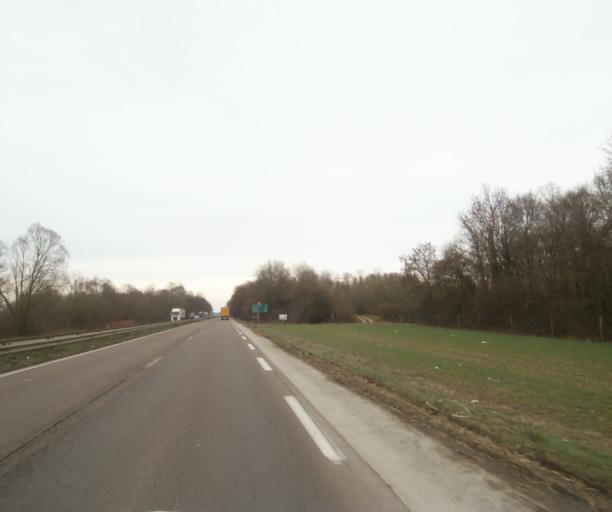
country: FR
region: Champagne-Ardenne
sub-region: Departement de la Haute-Marne
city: Villiers-en-Lieu
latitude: 48.6522
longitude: 4.8393
